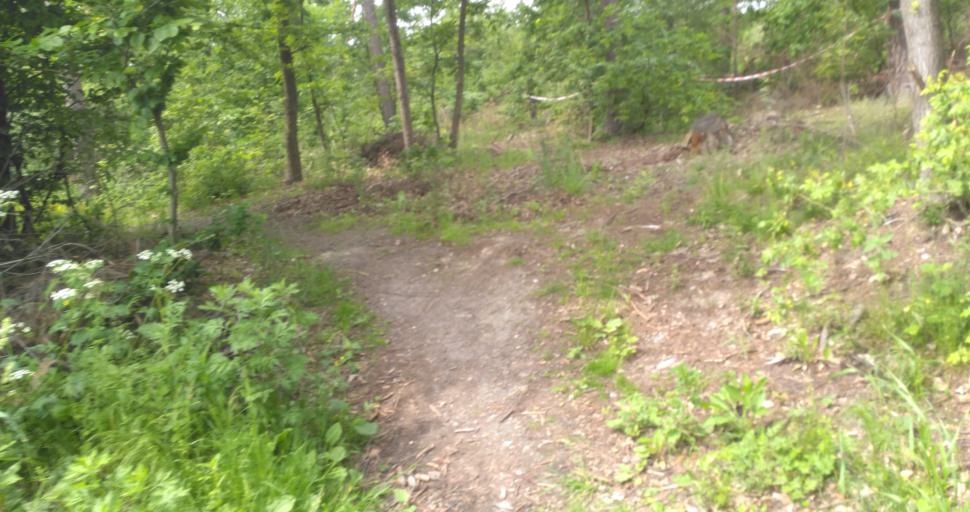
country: CZ
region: South Moravian
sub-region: Okres Blansko
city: Jedovnice
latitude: 49.3336
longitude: 16.7186
